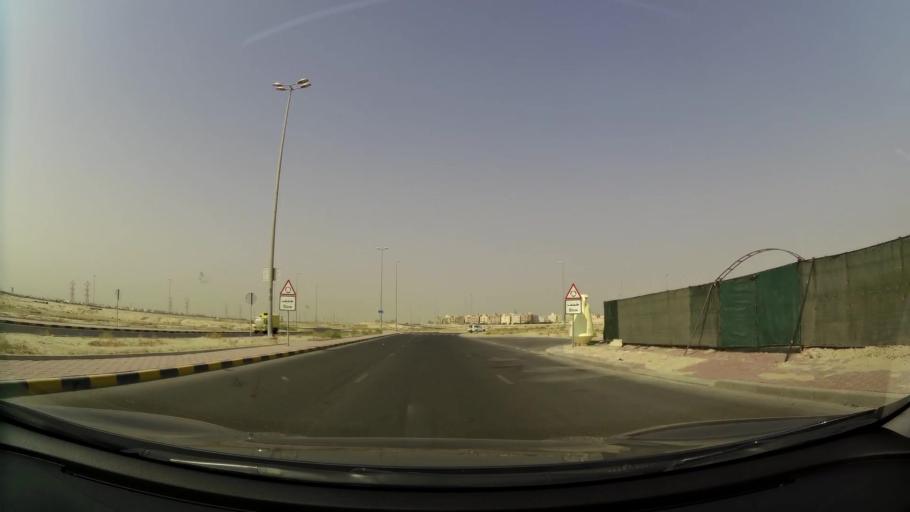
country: KW
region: Muhafazat al Jahra'
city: Al Jahra'
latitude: 29.3281
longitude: 47.7683
